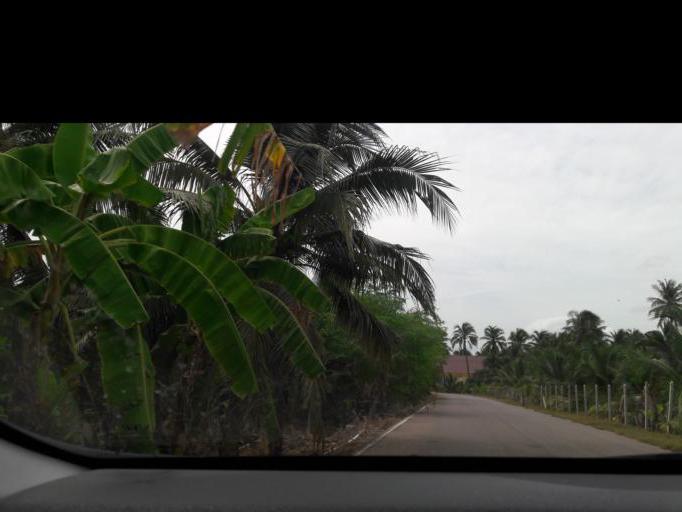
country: TH
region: Ratchaburi
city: Damnoen Saduak
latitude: 13.5573
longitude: 99.9908
